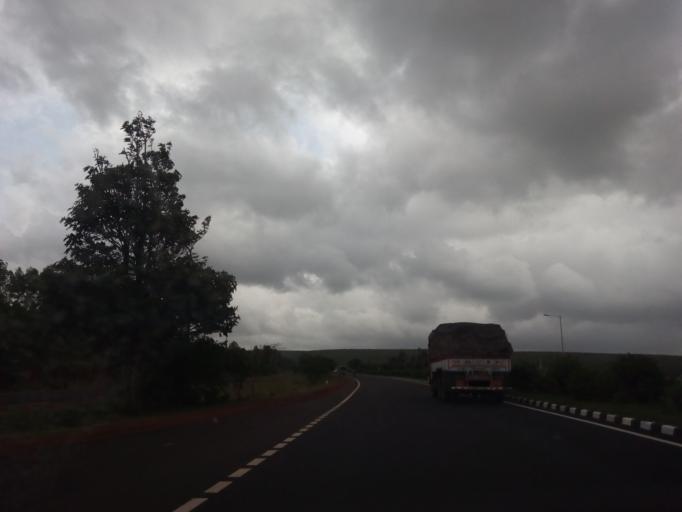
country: IN
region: Karnataka
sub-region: Belgaum
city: Hukeri
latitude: 16.0607
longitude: 74.5141
